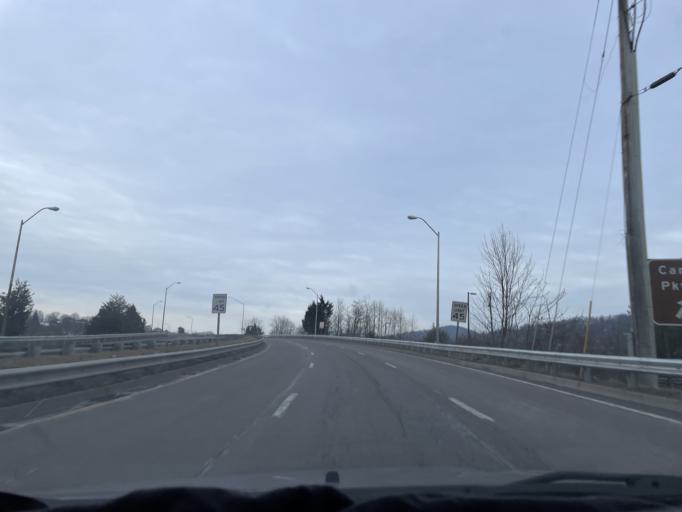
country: US
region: Maryland
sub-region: Allegany County
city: Cumberland
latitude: 39.6450
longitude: -78.7628
